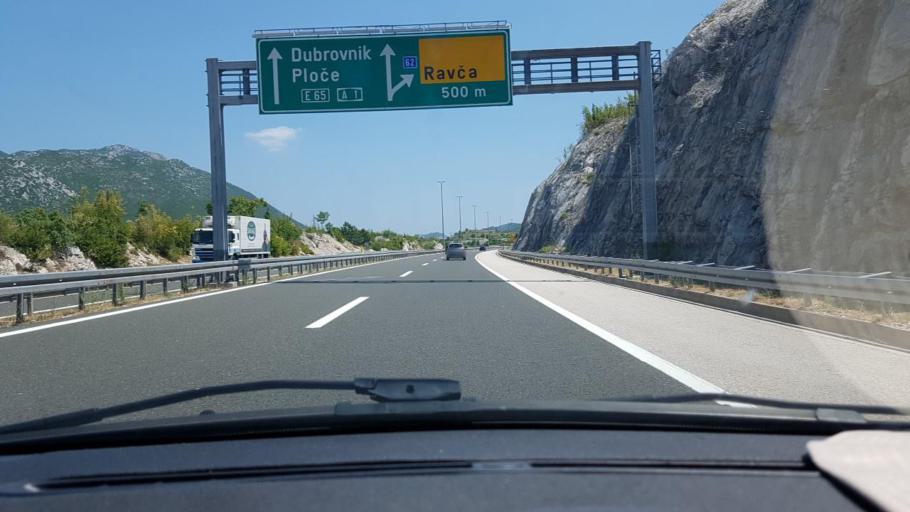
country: HR
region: Splitsko-Dalmatinska
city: Vrgorac
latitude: 43.2225
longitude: 17.2567
